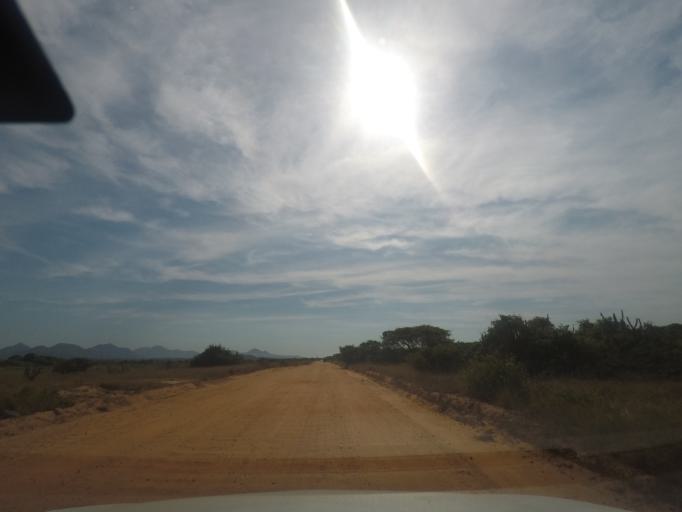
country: BR
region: Rio de Janeiro
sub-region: Marica
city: Marica
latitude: -22.9606
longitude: -42.8537
